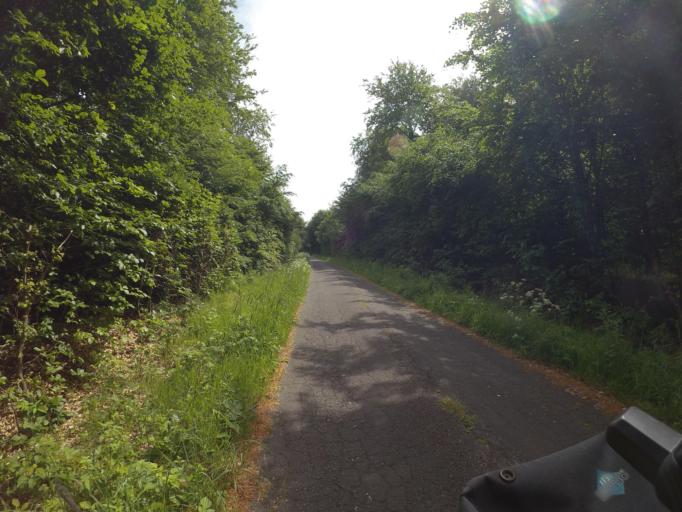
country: DE
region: Rheinland-Pfalz
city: Damflos
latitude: 49.6816
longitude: 7.0025
